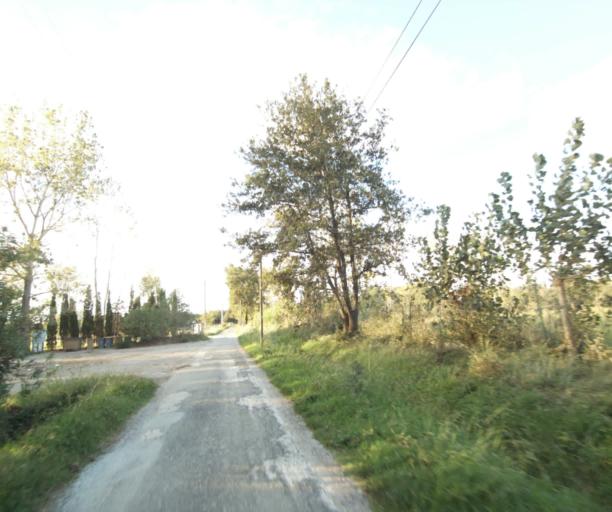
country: FR
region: Languedoc-Roussillon
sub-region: Departement des Pyrenees-Orientales
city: Sant Andreu de Sureda
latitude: 42.5733
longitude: 2.9864
